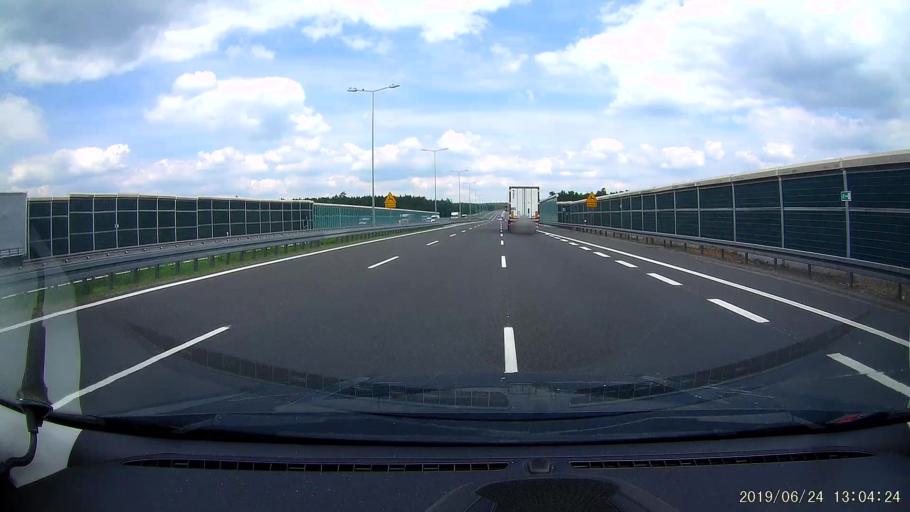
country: PL
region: Silesian Voivodeship
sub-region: Powiat rybnicki
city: Stanowice
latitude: 50.0831
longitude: 18.6636
